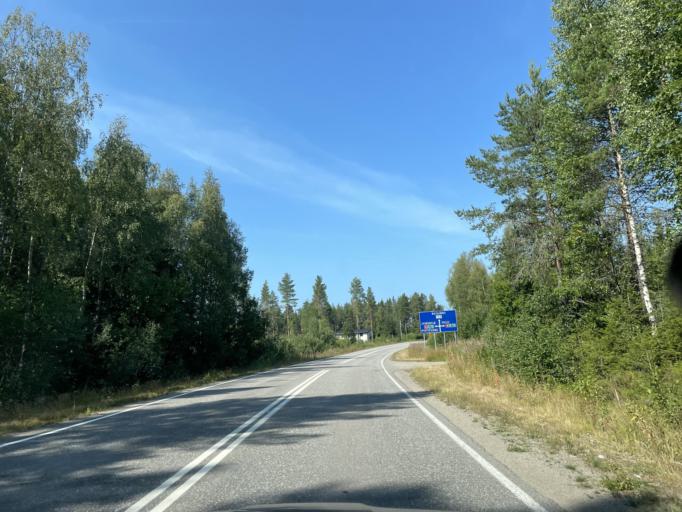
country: FI
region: Central Finland
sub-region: Saarijaervi-Viitasaari
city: Pihtipudas
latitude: 63.3750
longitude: 25.5978
